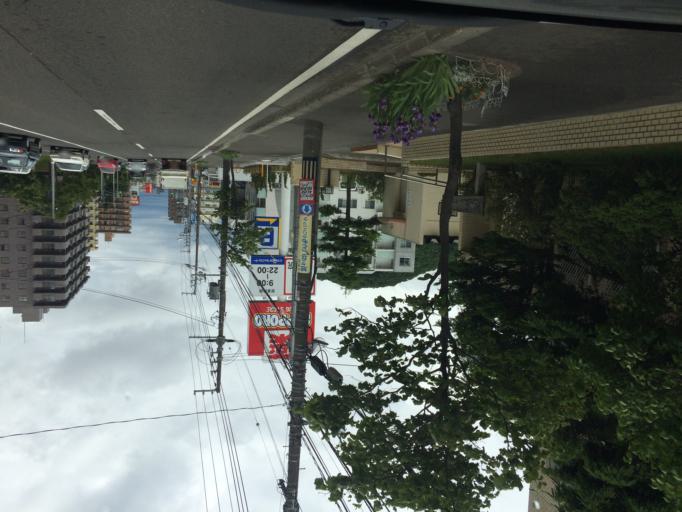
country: JP
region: Hokkaido
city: Sapporo
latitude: 43.0406
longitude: 141.3276
